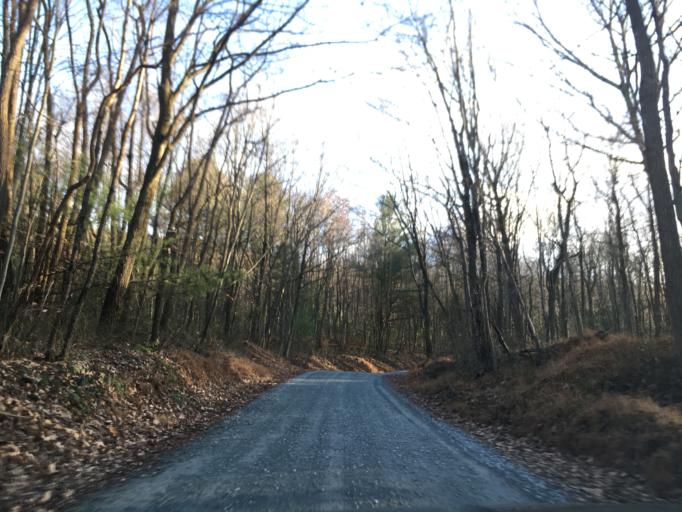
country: US
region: Pennsylvania
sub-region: Carbon County
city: Lehighton
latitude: 40.7705
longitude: -75.7105
